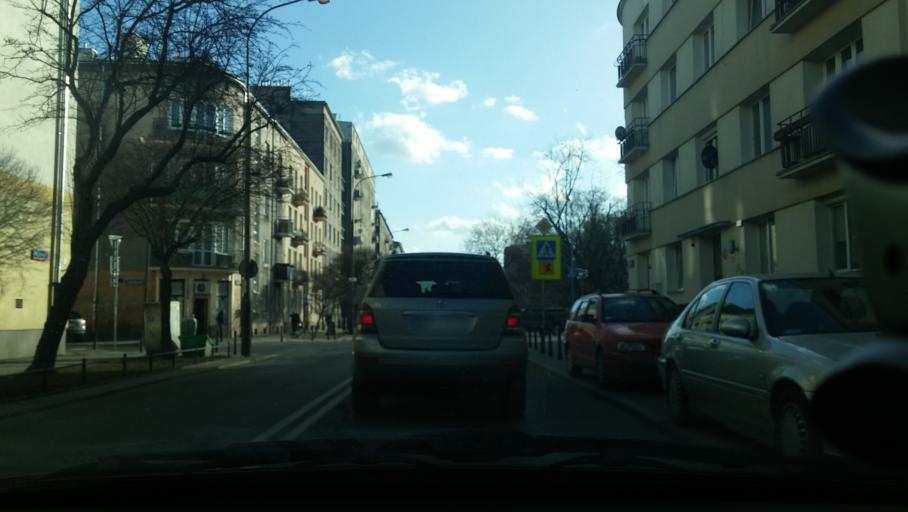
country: PL
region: Masovian Voivodeship
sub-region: Warszawa
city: Ochota
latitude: 52.2160
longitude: 20.9758
